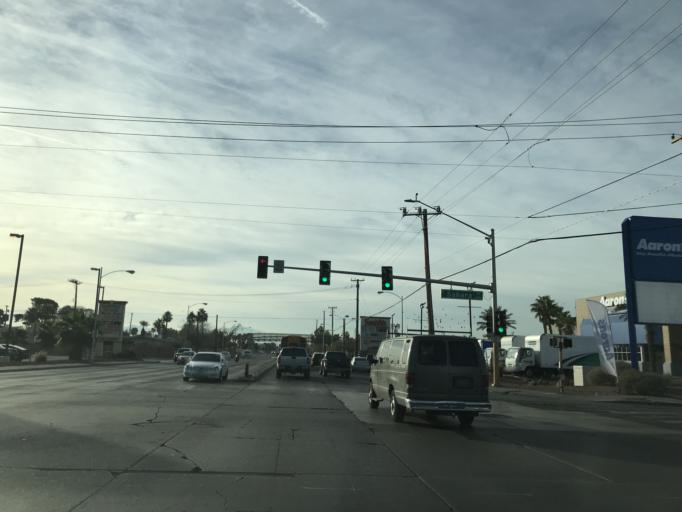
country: US
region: Nevada
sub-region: Clark County
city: Winchester
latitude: 36.1444
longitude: -115.0655
